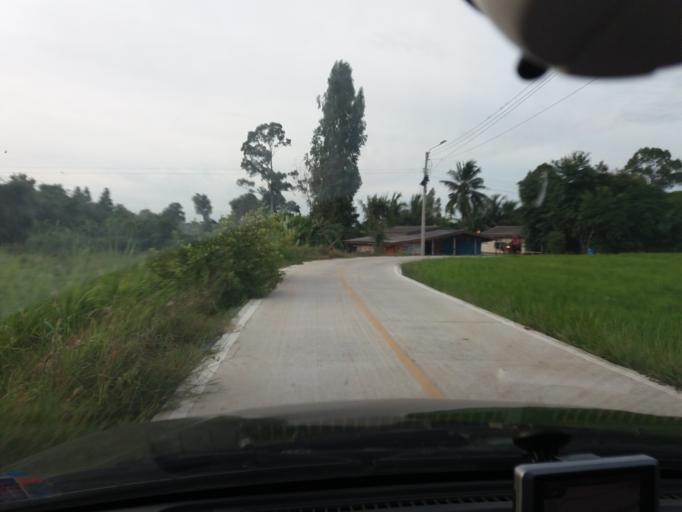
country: TH
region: Suphan Buri
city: Doembang Nangbuat
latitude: 14.8297
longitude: 100.1406
